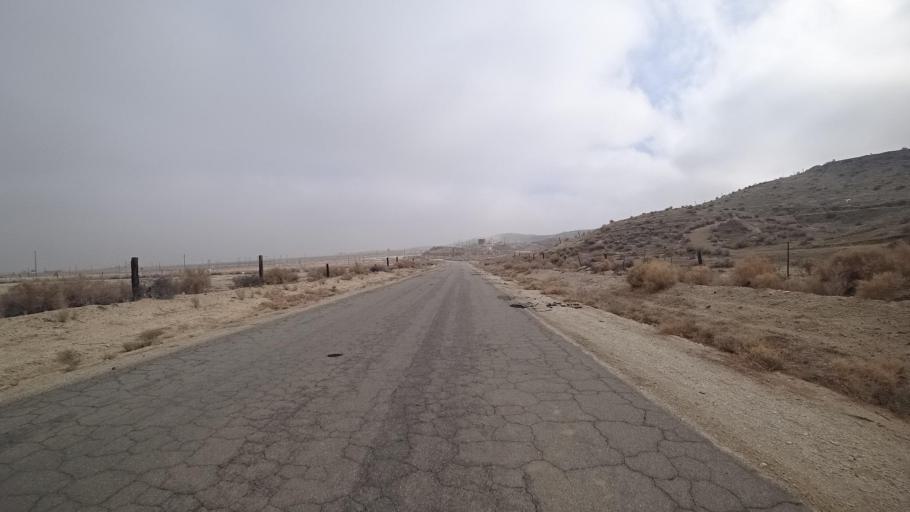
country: US
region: California
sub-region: Kern County
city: Maricopa
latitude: 35.0389
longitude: -119.3815
